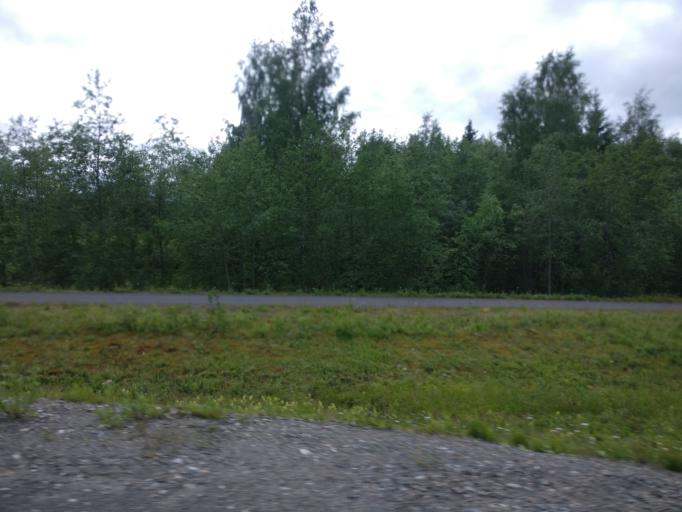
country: FI
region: Northern Savo
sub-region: Kuopio
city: Vehmersalmi
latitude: 62.9397
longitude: 27.9105
